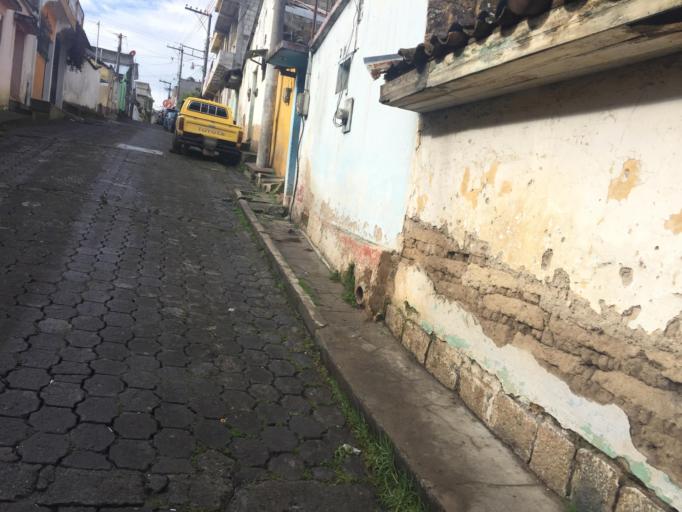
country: GT
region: Totonicapan
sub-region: Municipio de Totonicapan
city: Totonicapan
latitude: 14.9131
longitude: -91.3575
